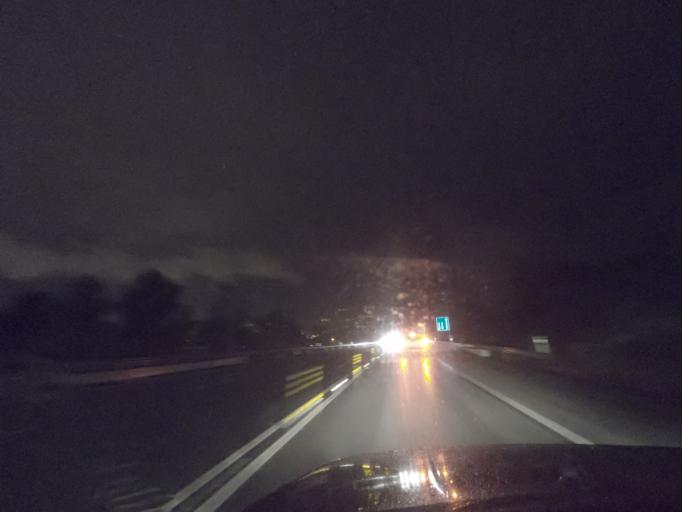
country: PT
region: Vila Real
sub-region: Vila Real
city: Vila Real
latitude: 41.3162
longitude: -7.7092
